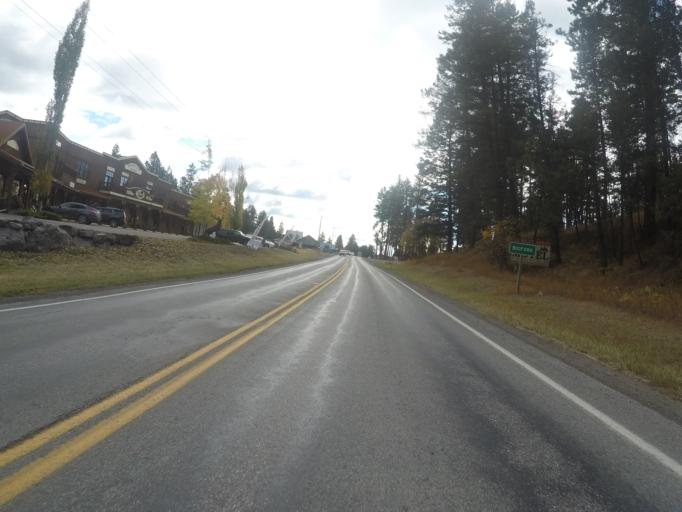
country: US
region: Montana
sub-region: Flathead County
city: Bigfork
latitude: 48.0799
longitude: -114.0790
